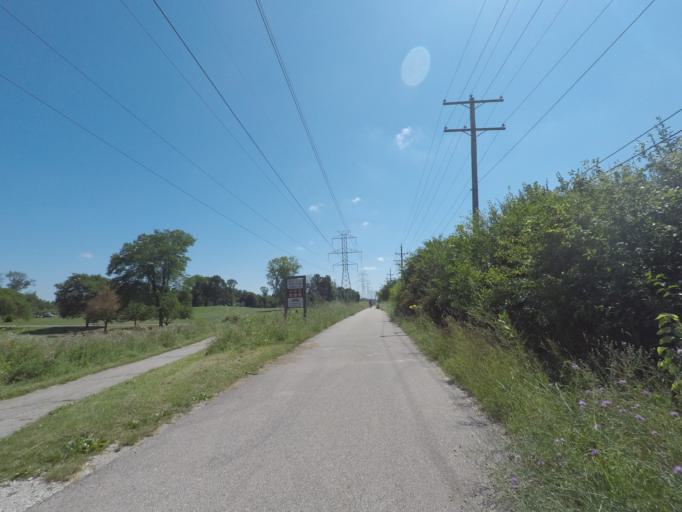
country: US
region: Wisconsin
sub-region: Waukesha County
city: Elm Grove
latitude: 43.0103
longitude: -88.0647
